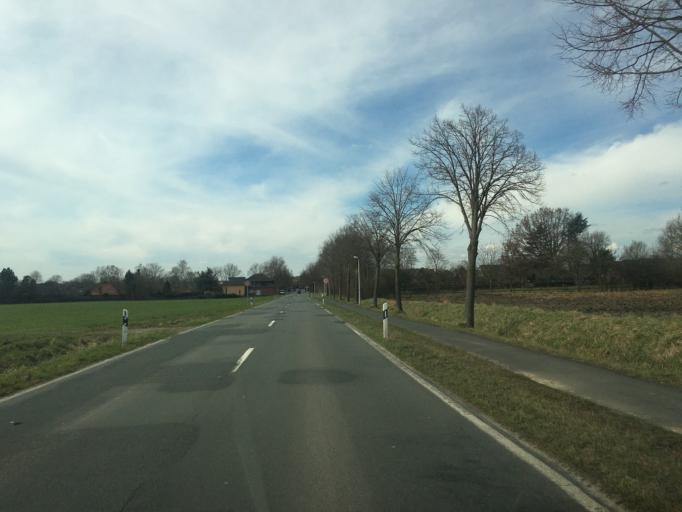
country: DE
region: North Rhine-Westphalia
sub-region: Regierungsbezirk Munster
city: Ascheberg
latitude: 51.7319
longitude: 7.6026
